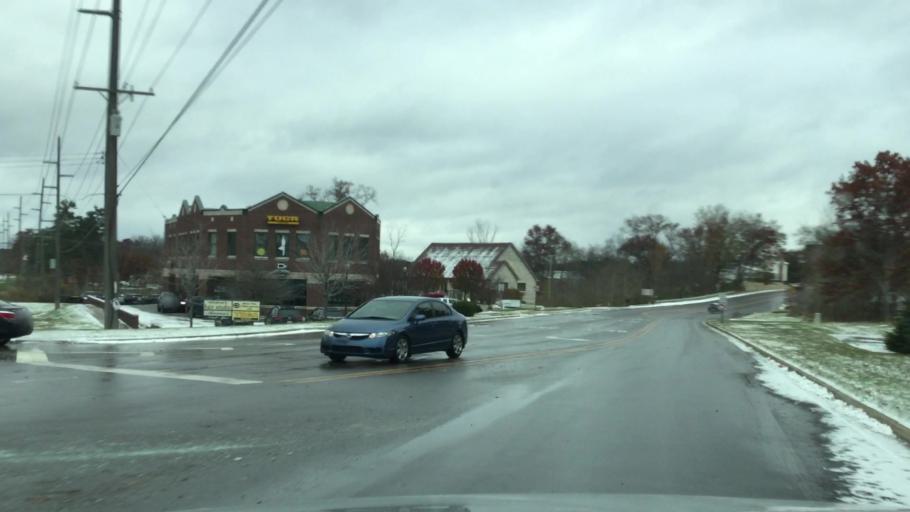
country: US
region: Michigan
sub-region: Livingston County
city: Brighton
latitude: 42.5365
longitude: -83.7543
